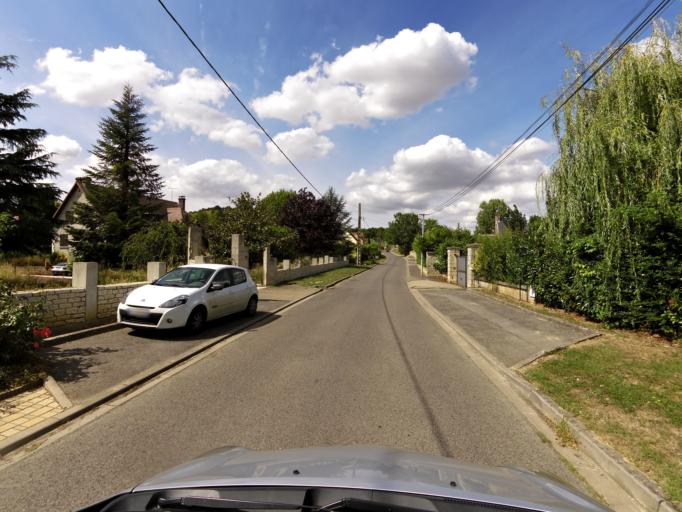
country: FR
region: Picardie
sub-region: Departement de l'Aisne
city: Courmelles
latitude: 49.3409
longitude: 3.3102
